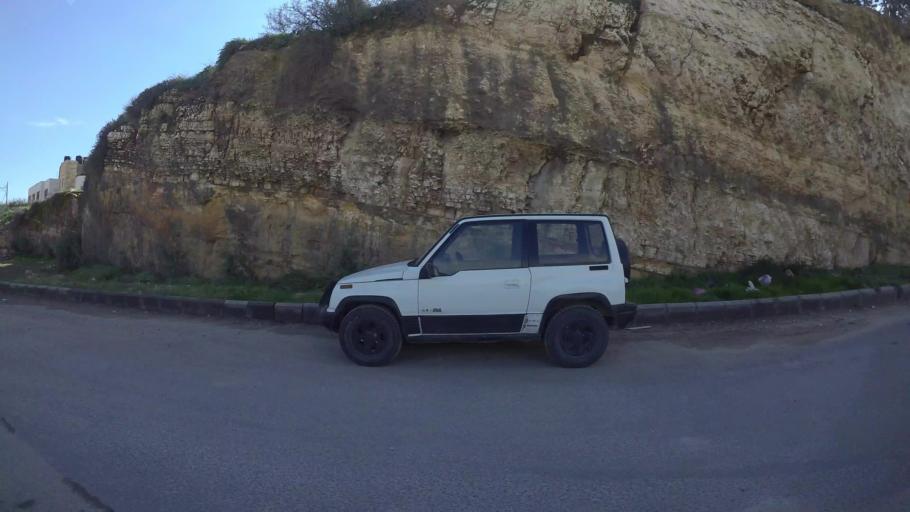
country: JO
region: Amman
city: Al Jubayhah
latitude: 32.0139
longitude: 35.8464
